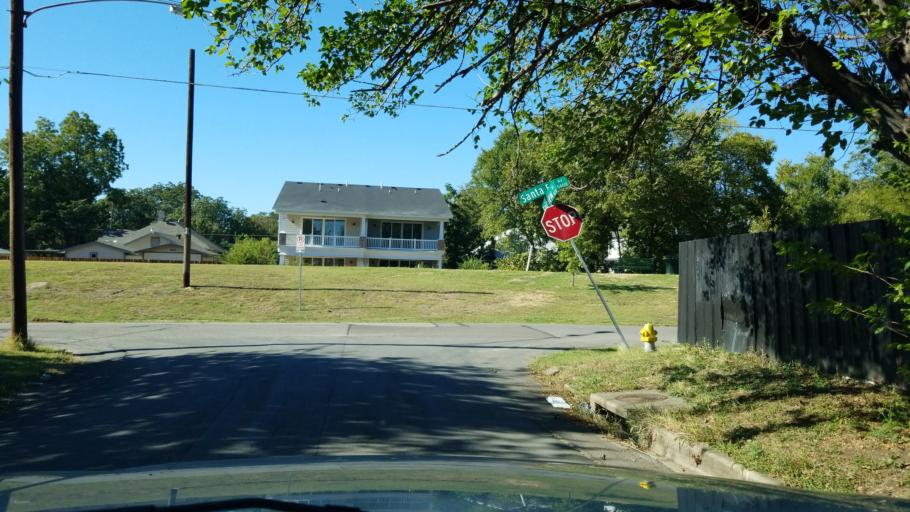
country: US
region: Texas
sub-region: Dallas County
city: Highland Park
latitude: 32.7975
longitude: -96.7560
